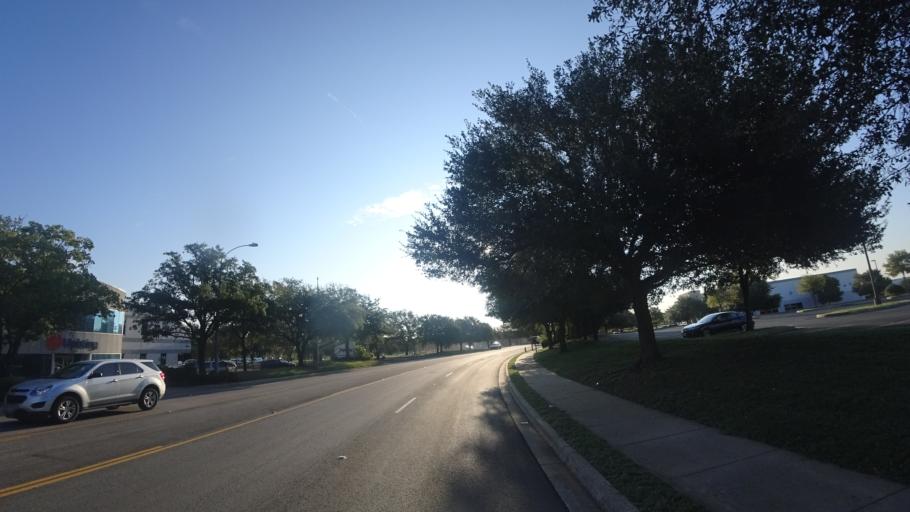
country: US
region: Texas
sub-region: Travis County
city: Austin
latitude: 30.3356
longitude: -97.6702
